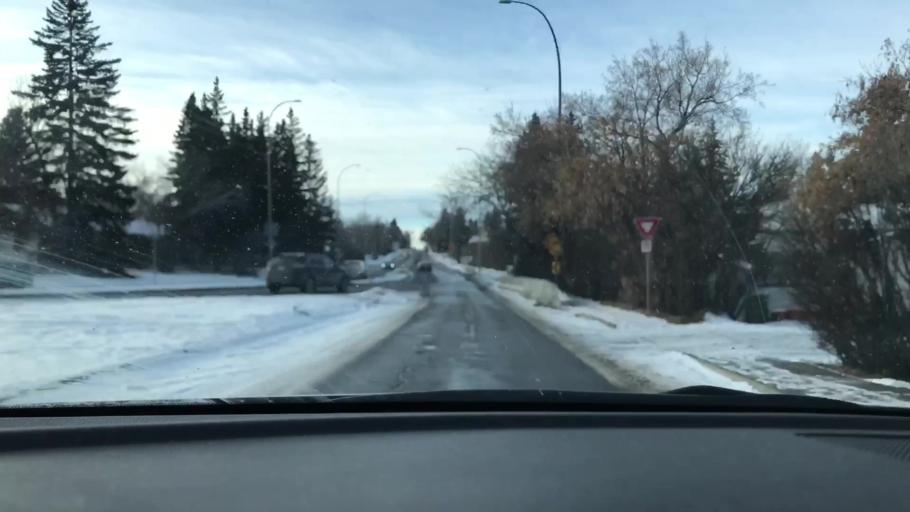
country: CA
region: Alberta
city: Calgary
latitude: 51.0258
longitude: -114.1301
